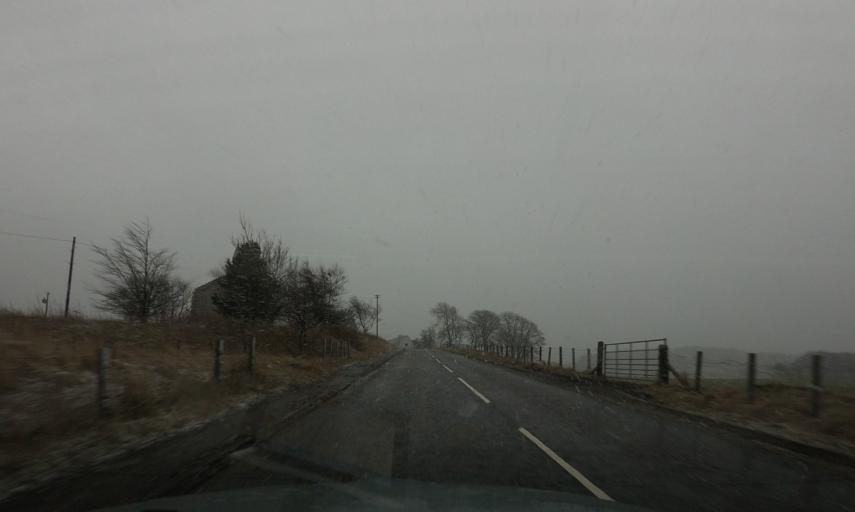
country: GB
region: Scotland
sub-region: North Lanarkshire
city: Caldercruix
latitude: 55.8455
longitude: -3.8517
